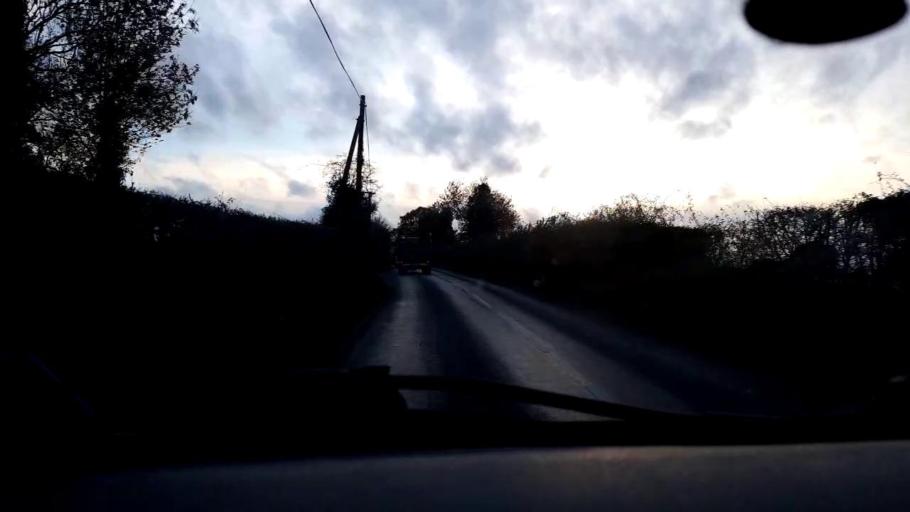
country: GB
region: England
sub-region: Norfolk
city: Mattishall
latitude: 52.7031
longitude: 1.1021
